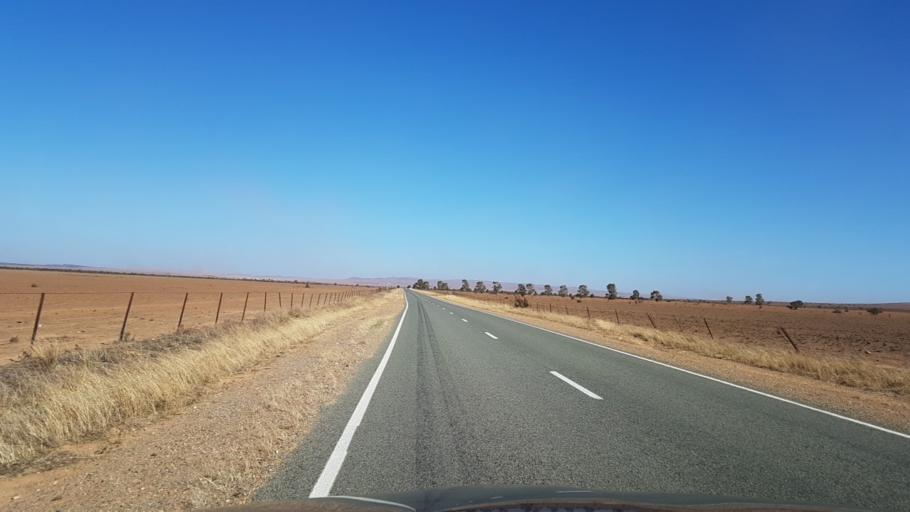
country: AU
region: South Australia
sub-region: Peterborough
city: Peterborough
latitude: -33.1092
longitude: 138.9265
